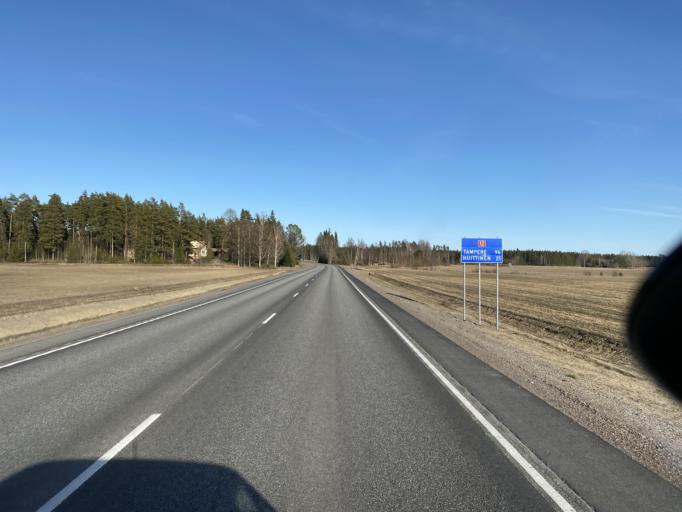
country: FI
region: Satakunta
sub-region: Rauma
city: Koeylioe
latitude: 61.1627
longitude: 22.3228
